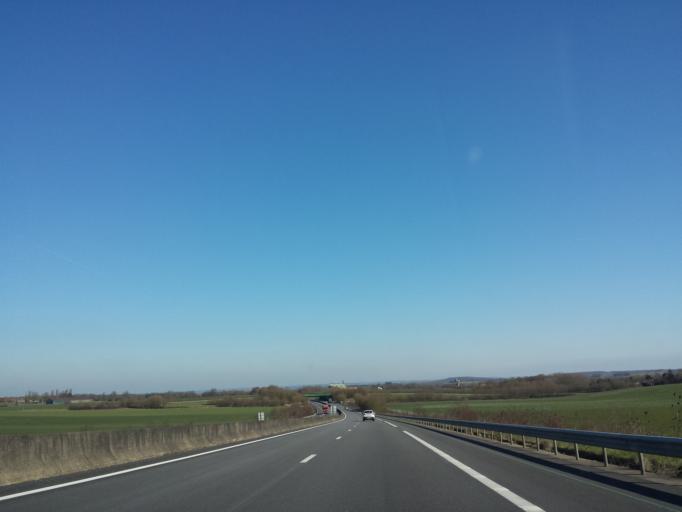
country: FR
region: Picardie
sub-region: Departement de l'Oise
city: Saint-Sulpice
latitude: 49.3323
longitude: 2.0997
